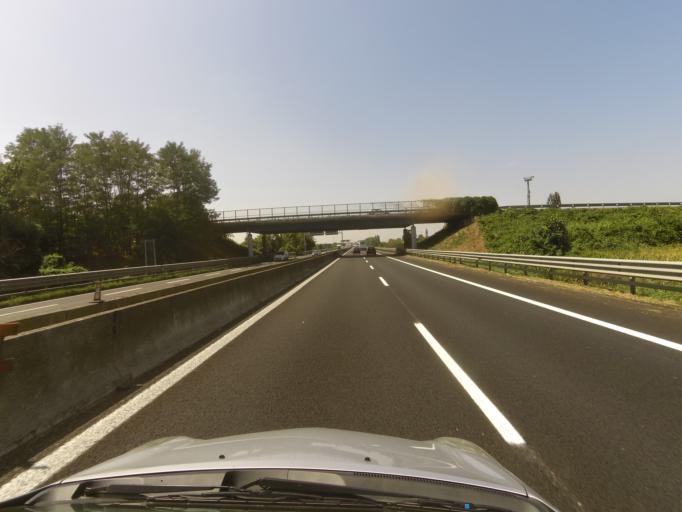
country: IT
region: Veneto
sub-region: Provincia di Rovigo
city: Occhiobello
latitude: 44.9230
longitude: 11.5906
